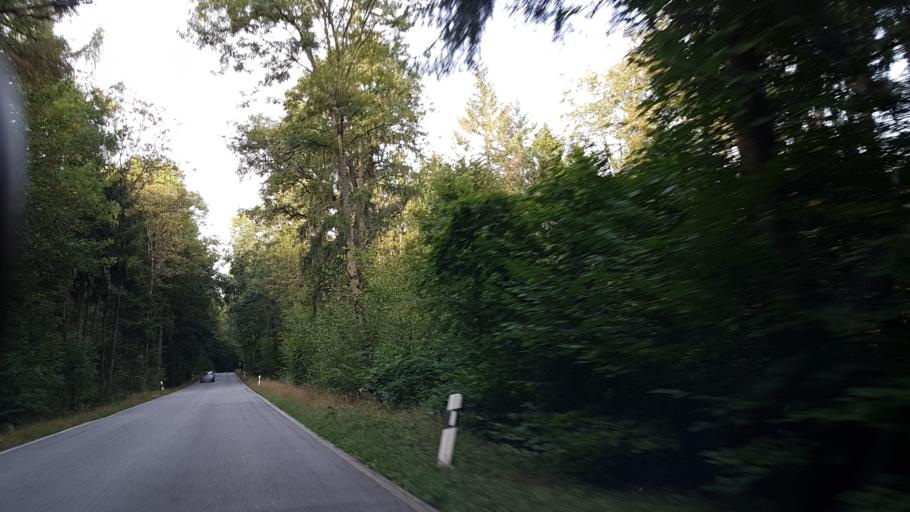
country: DE
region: Baden-Wuerttemberg
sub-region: Regierungsbezirk Stuttgart
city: Eberstadt
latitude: 49.1945
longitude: 9.3276
